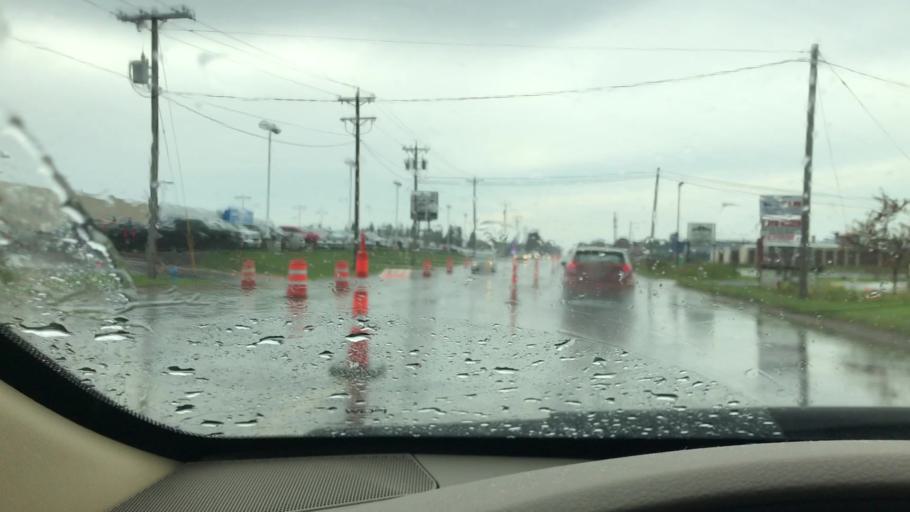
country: US
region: Minnesota
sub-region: Saint Louis County
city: Hermantown
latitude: 46.8221
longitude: -92.1804
